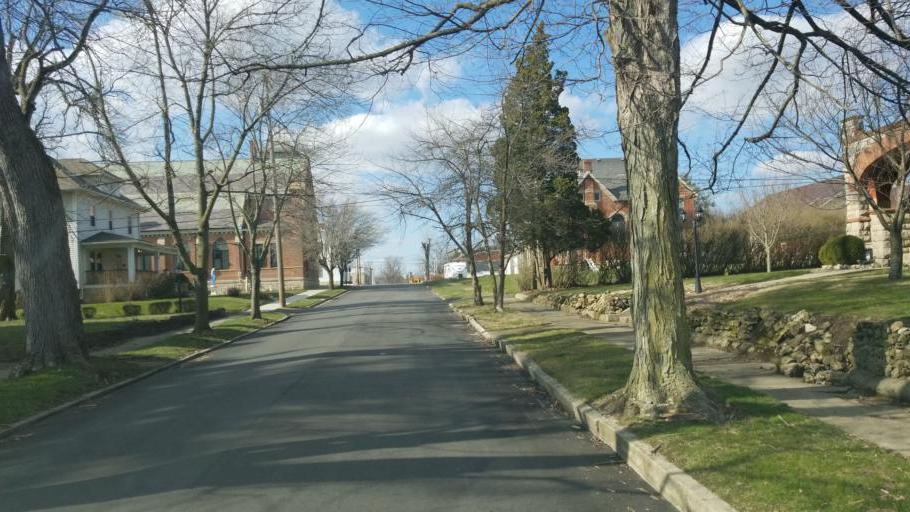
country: US
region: Ohio
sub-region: Highland County
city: Greenfield
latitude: 39.3501
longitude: -83.3803
